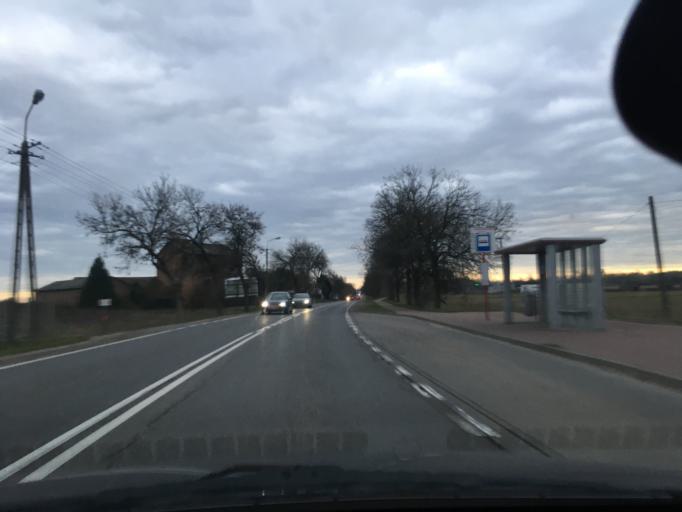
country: PL
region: Masovian Voivodeship
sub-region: Powiat piaseczynski
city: Lesznowola
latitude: 52.0956
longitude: 20.9242
